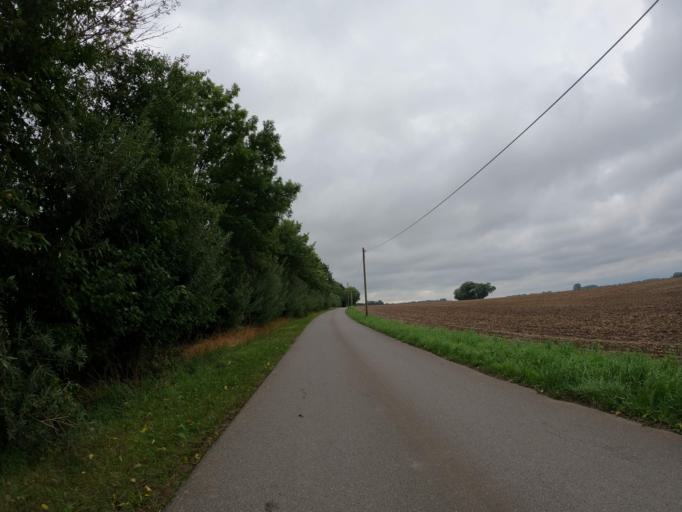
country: DE
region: Mecklenburg-Vorpommern
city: Garz
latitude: 54.3087
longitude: 13.3344
